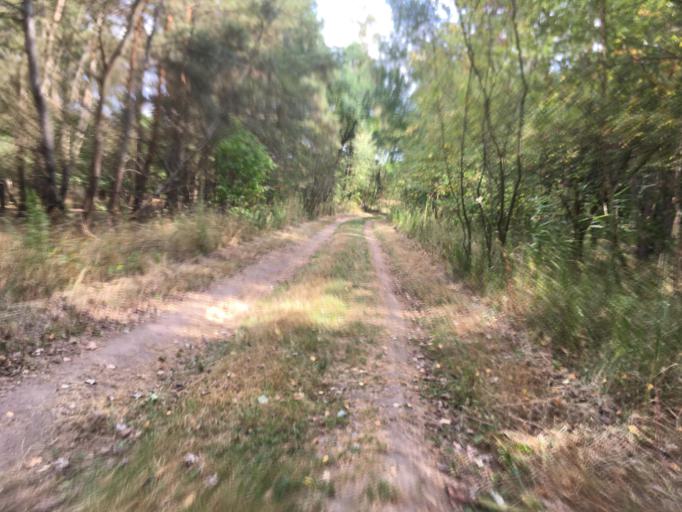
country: DE
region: Brandenburg
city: Zehdenick
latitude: 53.0563
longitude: 13.2888
